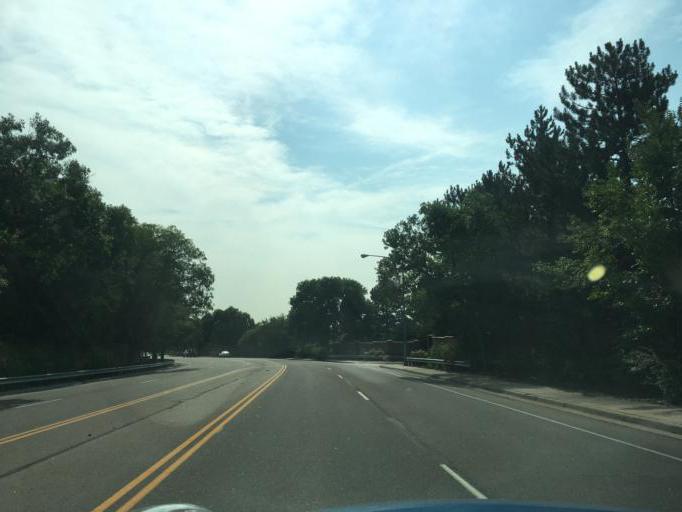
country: US
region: Colorado
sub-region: Adams County
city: Westminster
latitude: 39.8270
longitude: -105.0614
